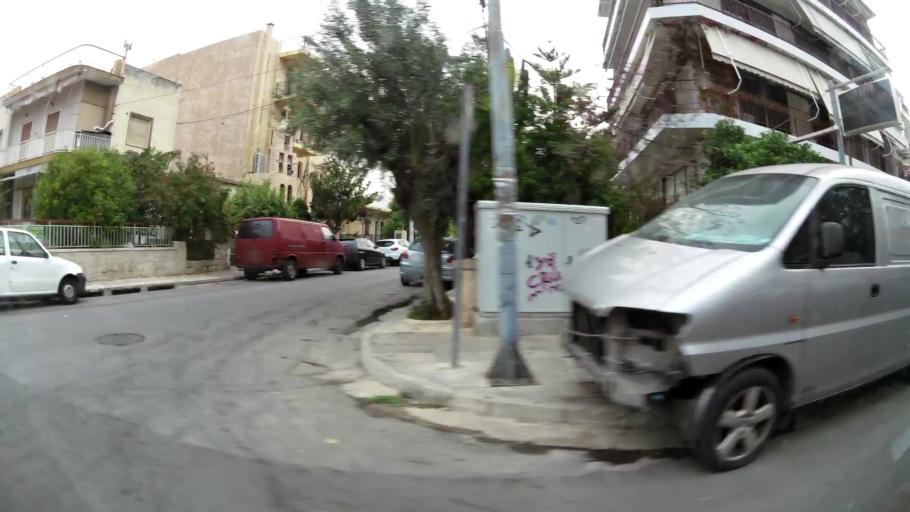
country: GR
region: Attica
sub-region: Nomarchia Athinas
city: Peristeri
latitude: 38.0098
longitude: 23.7051
